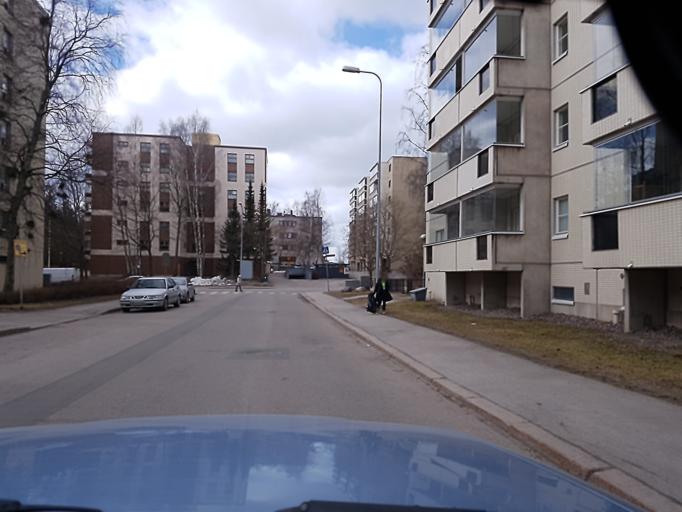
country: FI
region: Uusimaa
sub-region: Helsinki
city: Helsinki
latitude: 60.1487
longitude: 24.8831
